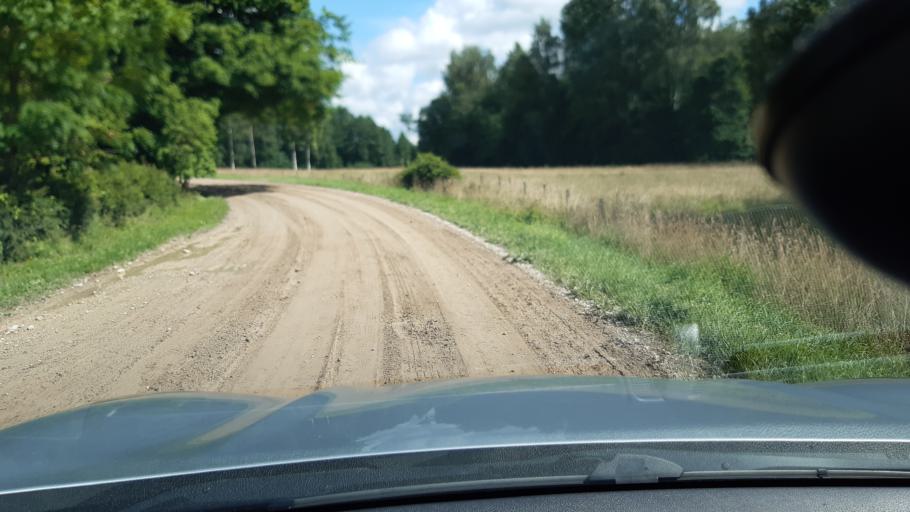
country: EE
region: Jaervamaa
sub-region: Tueri vald
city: Tueri
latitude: 58.9213
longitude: 25.1991
